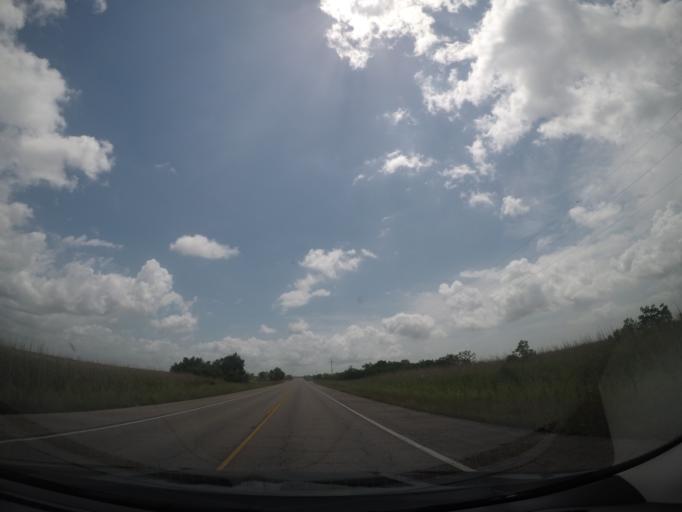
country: US
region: Mississippi
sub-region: Hancock County
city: Pearlington
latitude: 30.2366
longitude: -89.6319
